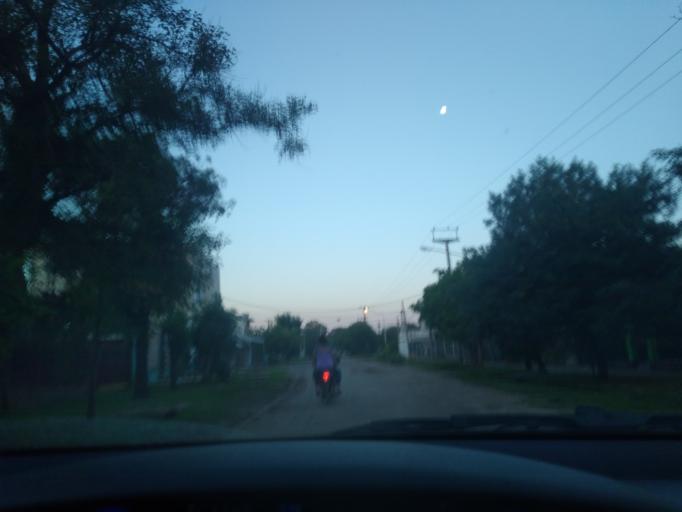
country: AR
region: Chaco
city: Barranqueras
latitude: -27.4749
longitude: -58.9324
